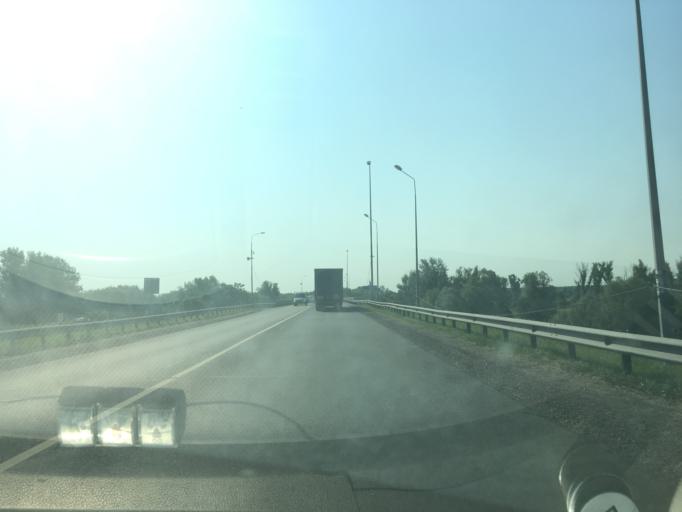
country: RU
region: Nizjnij Novgorod
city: Kstovo
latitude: 56.0988
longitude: 44.3084
